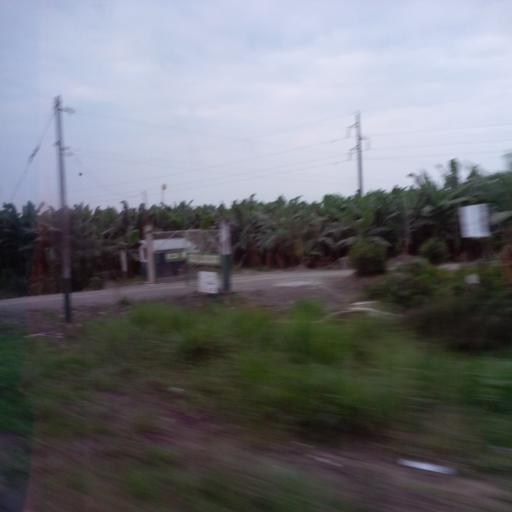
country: EC
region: Canar
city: La Troncal
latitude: -2.3451
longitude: -79.3683
